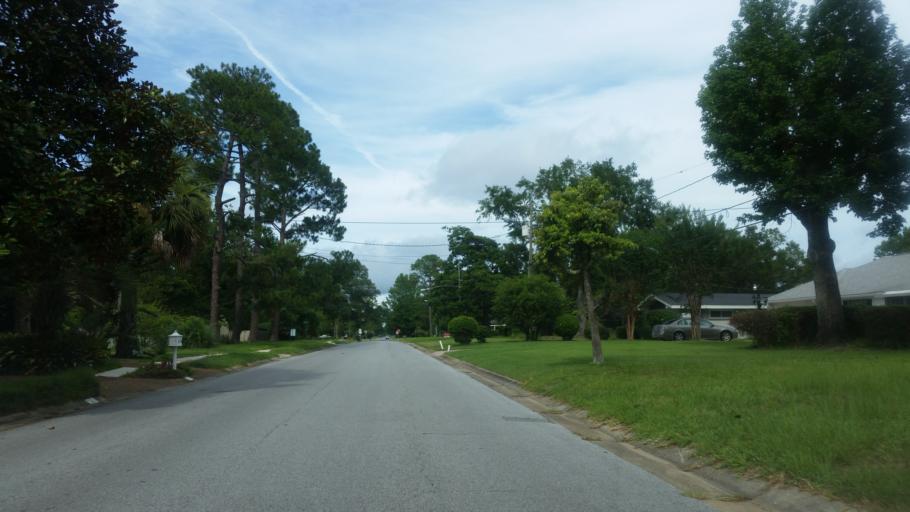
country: US
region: Florida
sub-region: Escambia County
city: Goulding
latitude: 30.4426
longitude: -87.2018
